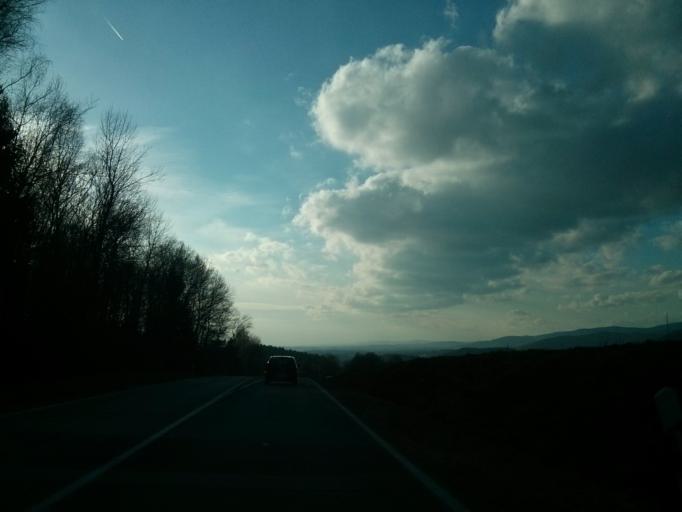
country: DE
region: Bavaria
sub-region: Lower Bavaria
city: Schaufling
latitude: 48.8398
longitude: 13.0153
